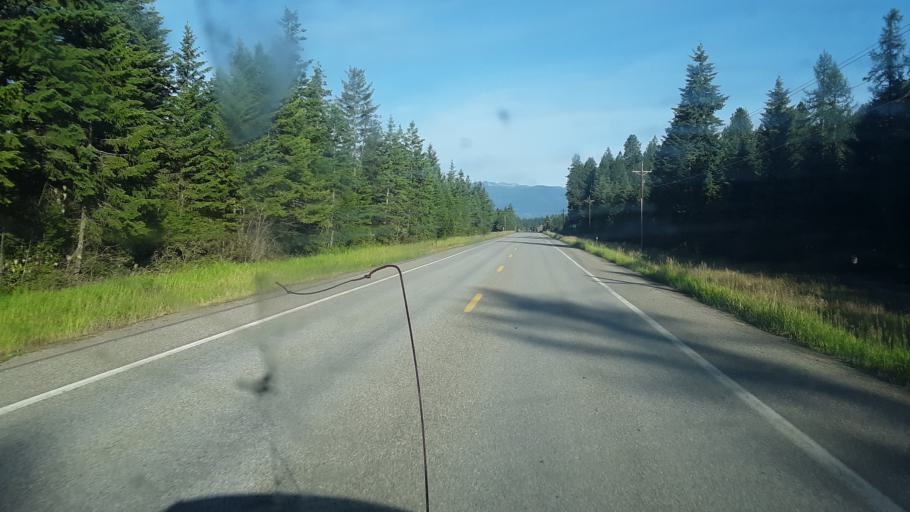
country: US
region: Idaho
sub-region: Boundary County
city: Bonners Ferry
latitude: 48.7275
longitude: -116.2179
